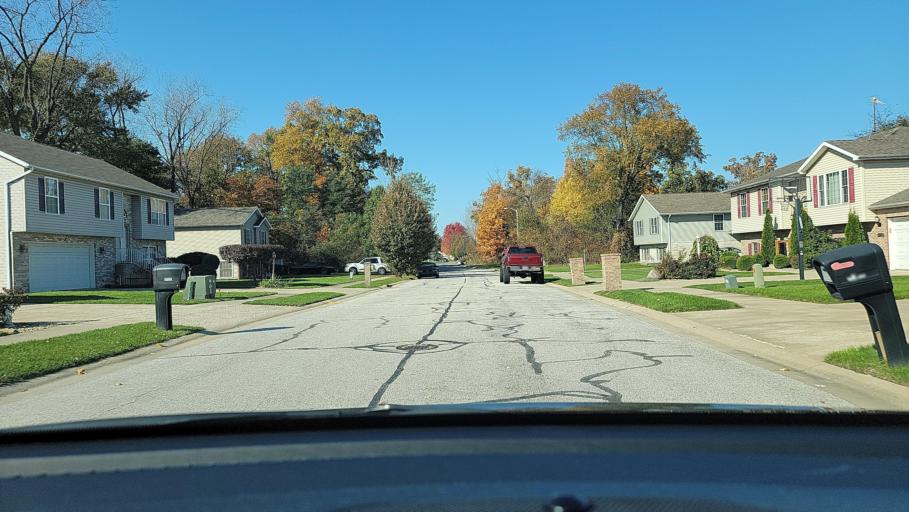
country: US
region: Indiana
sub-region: Porter County
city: Portage
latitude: 41.5774
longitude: -87.1568
